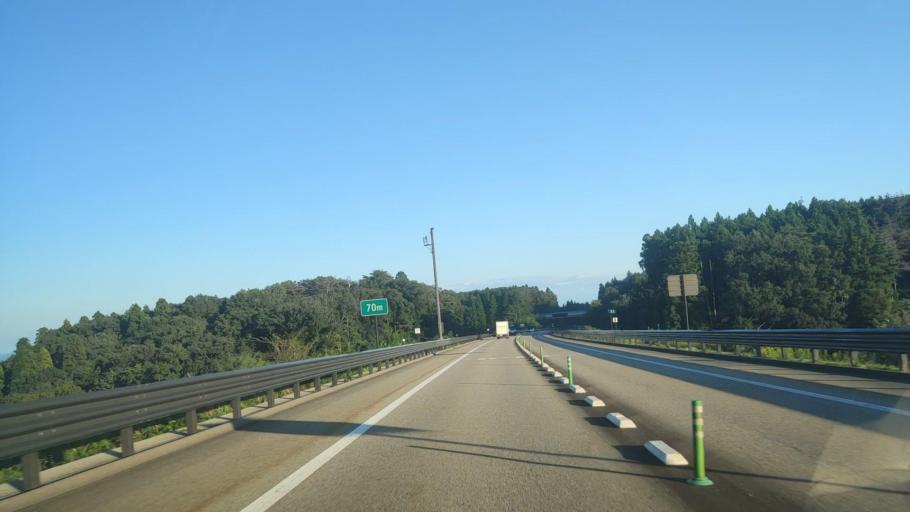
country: JP
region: Ishikawa
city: Nanao
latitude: 37.0061
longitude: 137.0374
